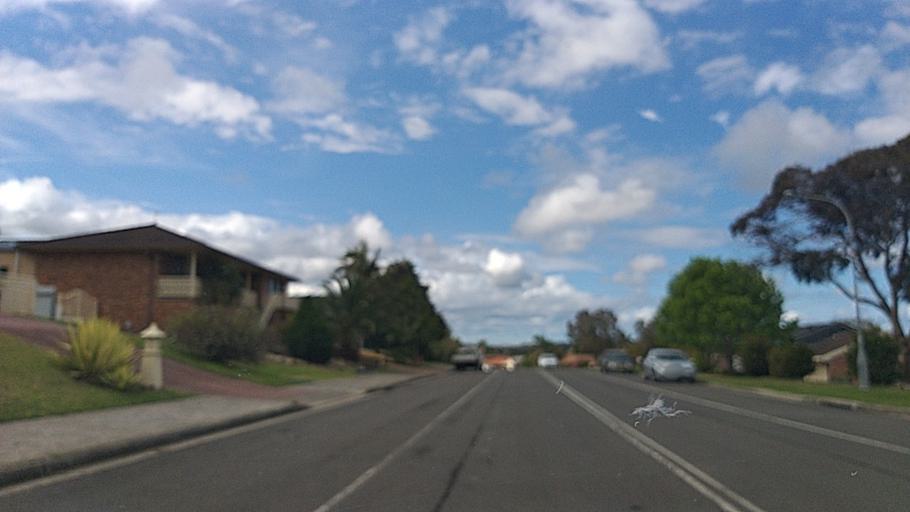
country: AU
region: New South Wales
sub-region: Wollongong
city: Dapto
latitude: -34.4937
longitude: 150.7802
